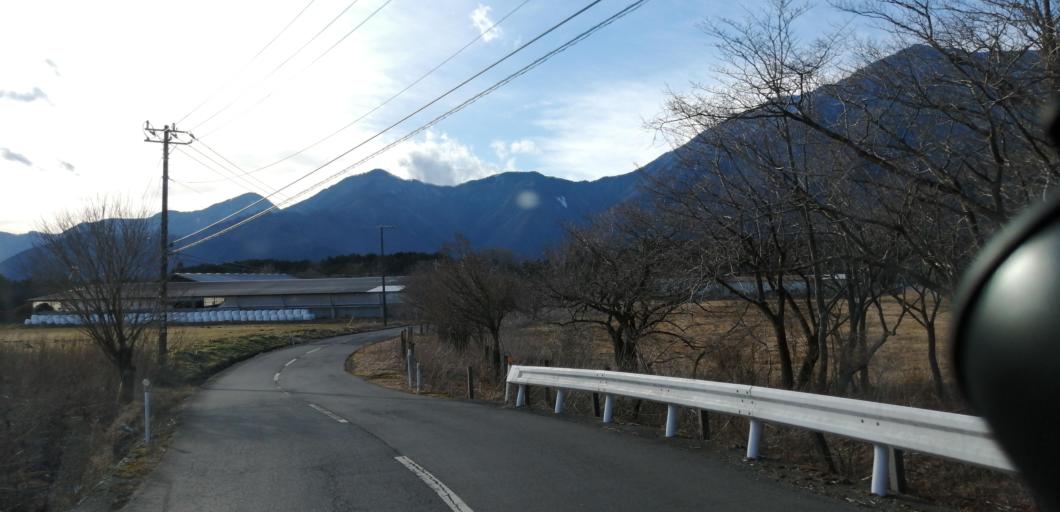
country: JP
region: Yamanashi
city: Fujikawaguchiko
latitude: 35.4045
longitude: 138.5917
